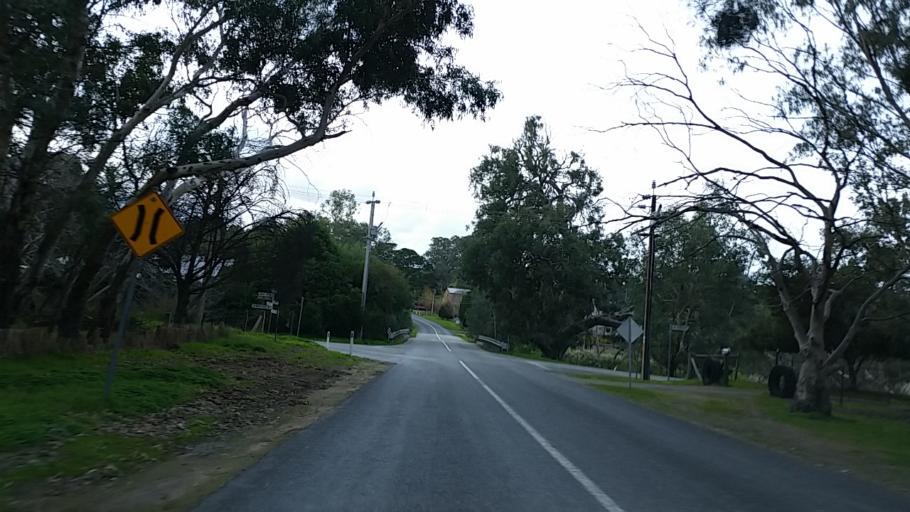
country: AU
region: South Australia
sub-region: Mount Barker
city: Nairne
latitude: -34.9508
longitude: 139.0130
